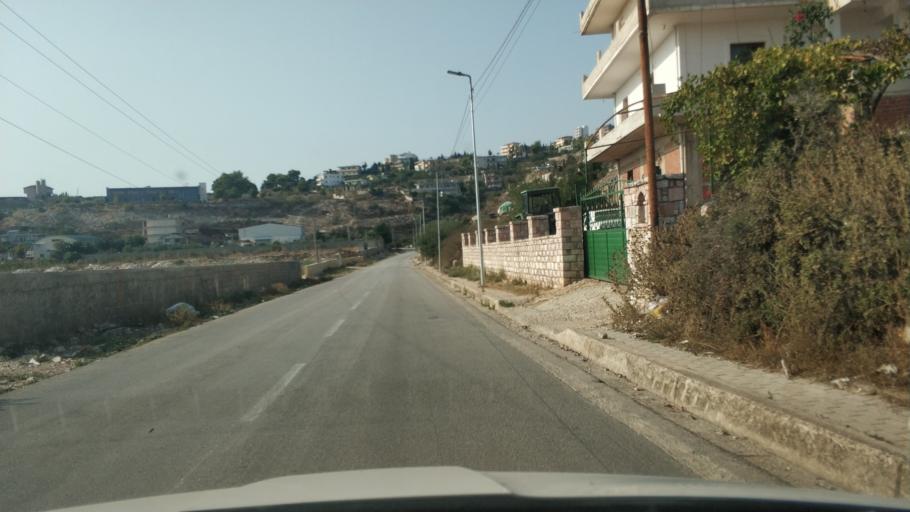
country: AL
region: Vlore
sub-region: Rrethi i Sarandes
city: Sarande
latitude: 39.8481
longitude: 20.0303
